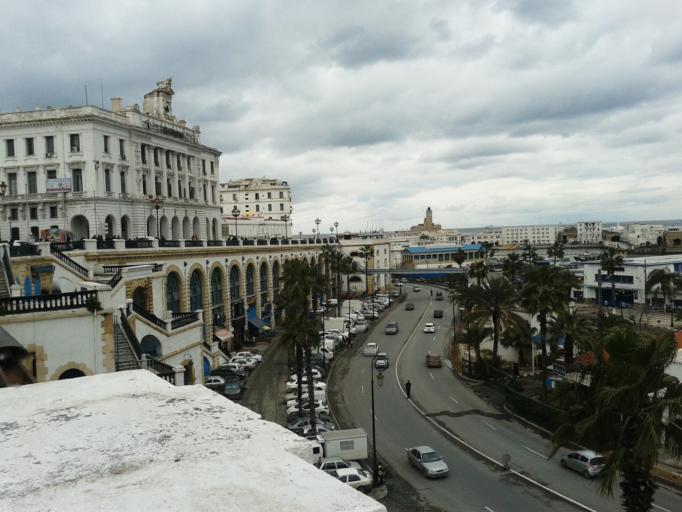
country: DZ
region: Alger
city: Algiers
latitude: 36.7839
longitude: 3.0630
